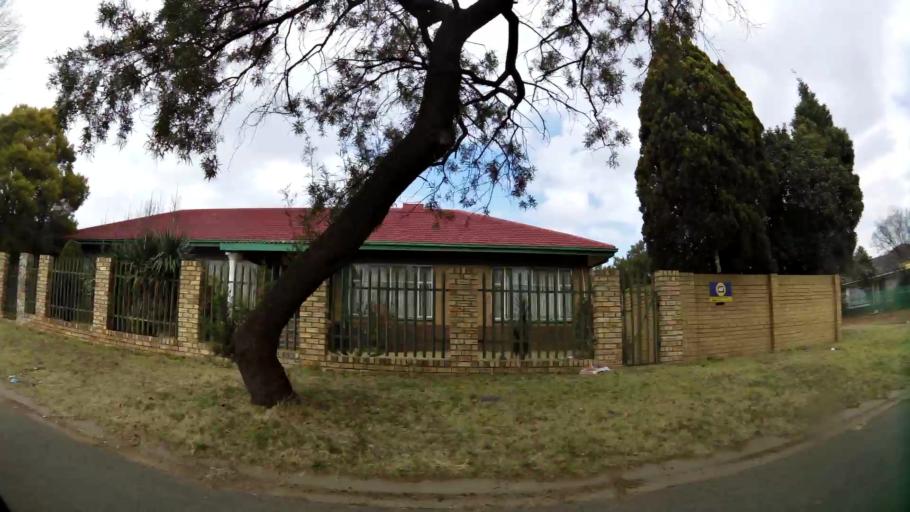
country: ZA
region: Gauteng
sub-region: Sedibeng District Municipality
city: Vanderbijlpark
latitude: -26.7144
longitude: 27.8582
